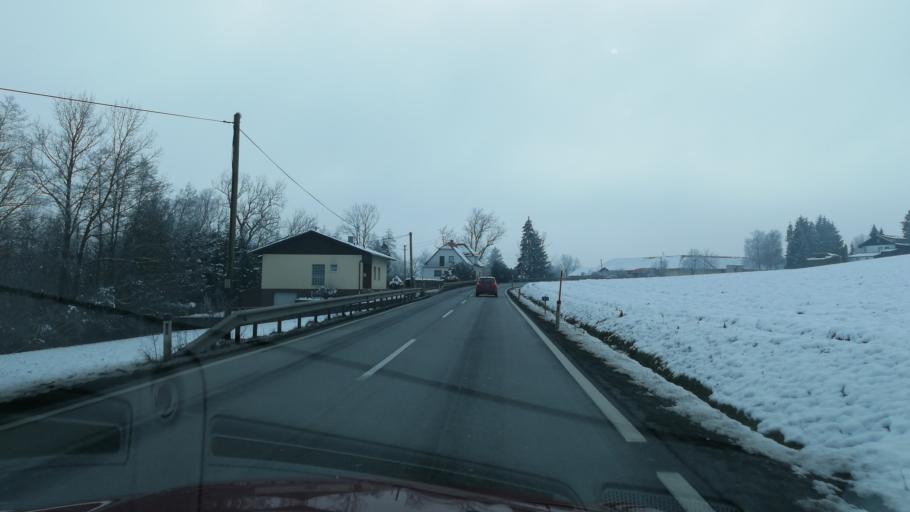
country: AT
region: Upper Austria
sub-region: Politischer Bezirk Grieskirchen
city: Bad Schallerbach
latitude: 48.2280
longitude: 13.9663
